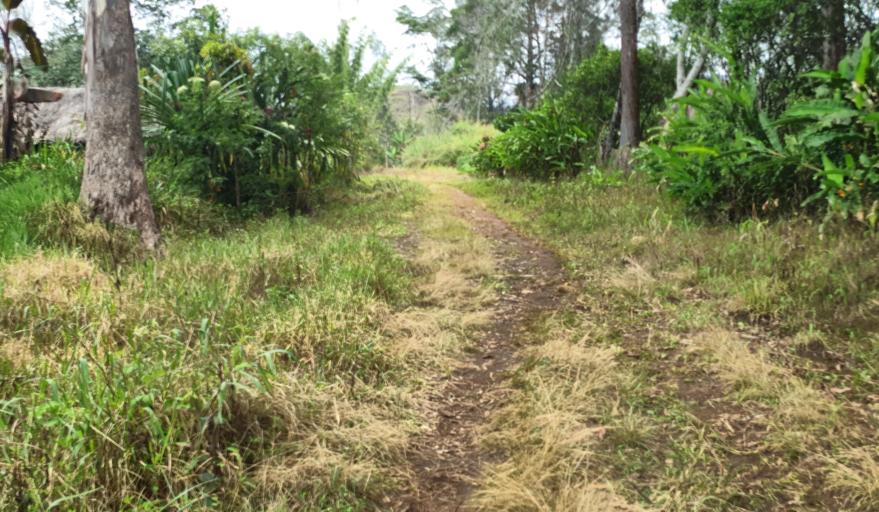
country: PG
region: Jiwaka
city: Minj
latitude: -5.9143
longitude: 144.8239
